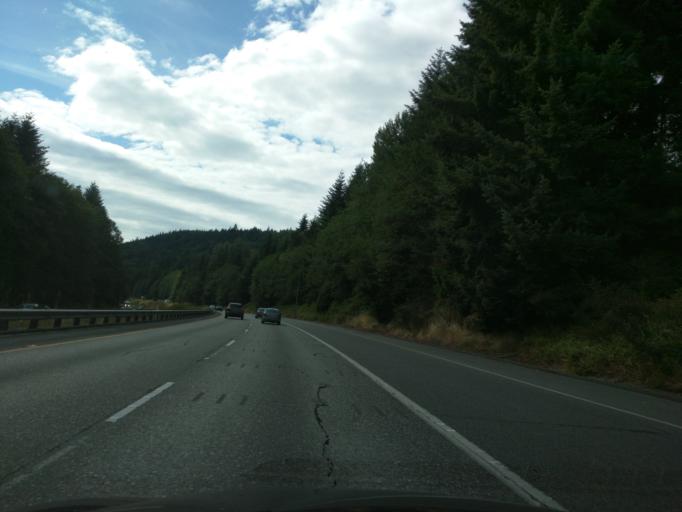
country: US
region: Washington
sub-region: Whatcom County
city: Geneva
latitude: 48.6897
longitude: -122.4048
